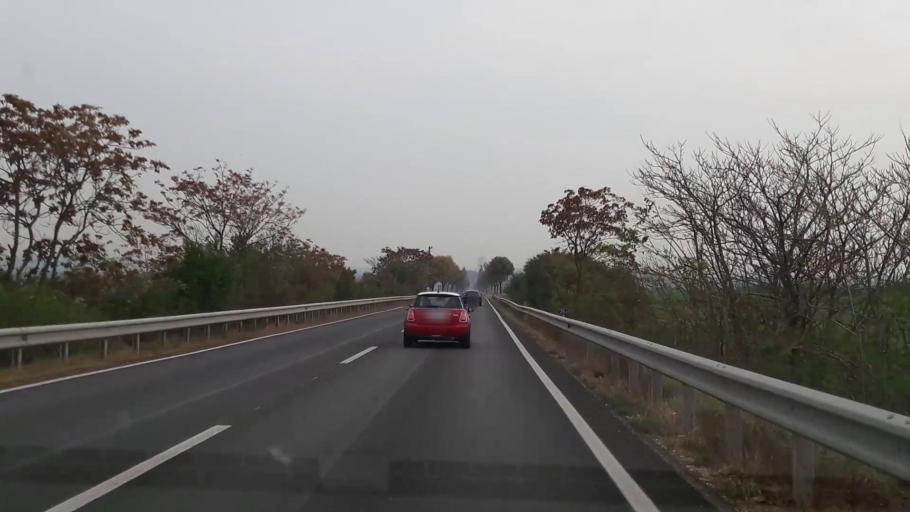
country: AT
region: Lower Austria
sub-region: Politischer Bezirk Wien-Umgebung
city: Schwadorf
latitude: 48.0825
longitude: 16.5662
